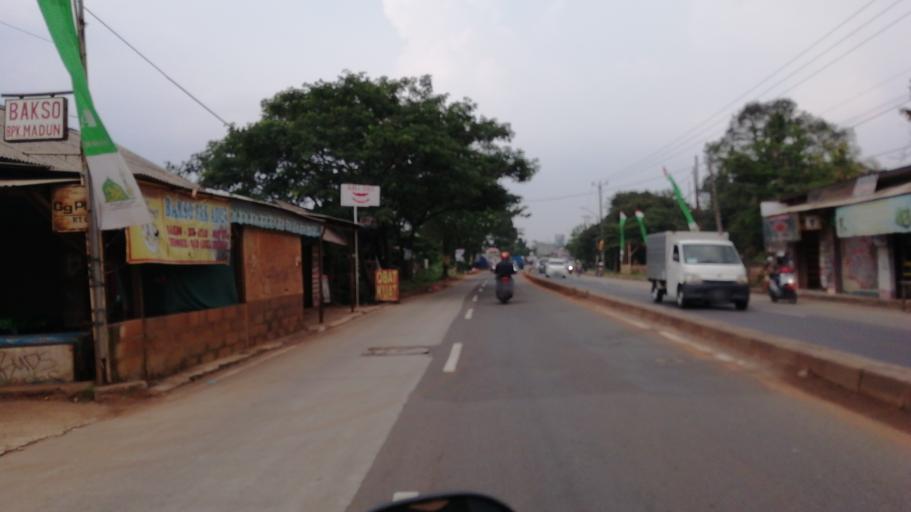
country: ID
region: West Java
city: Parung
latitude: -6.4668
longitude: 106.7291
